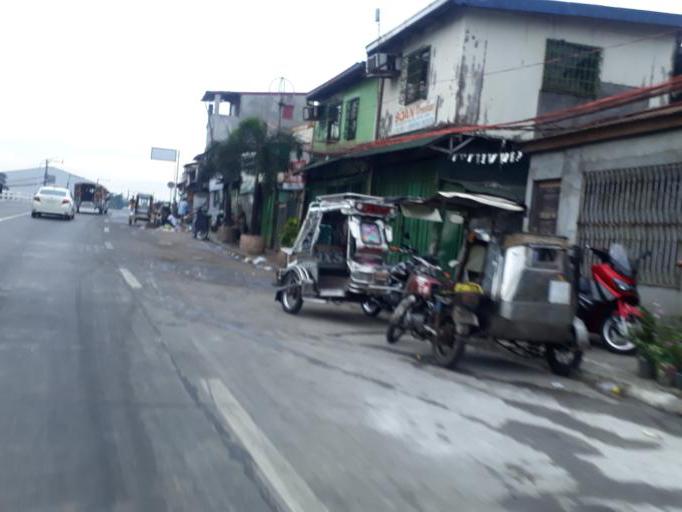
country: PH
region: Metro Manila
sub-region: Caloocan City
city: Niugan
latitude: 14.6530
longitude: 120.9530
